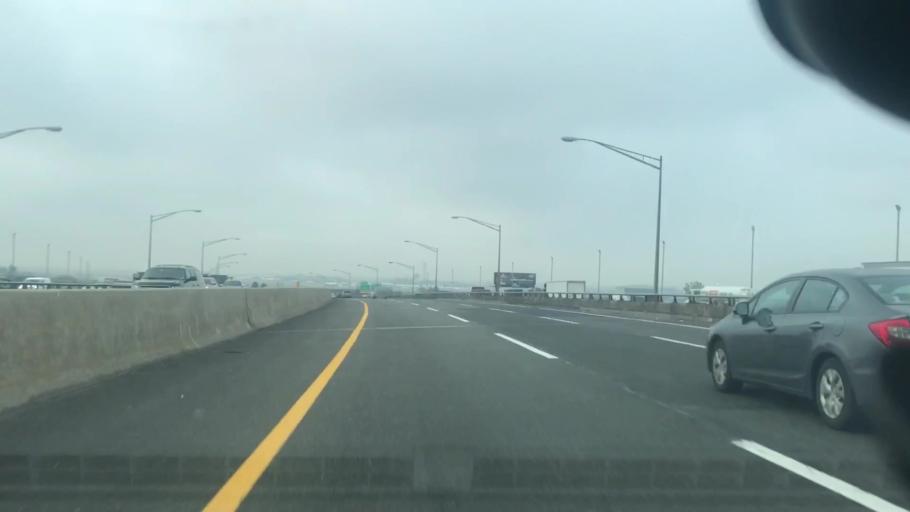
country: US
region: New Jersey
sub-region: Essex County
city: Newark
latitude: 40.7109
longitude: -74.1473
